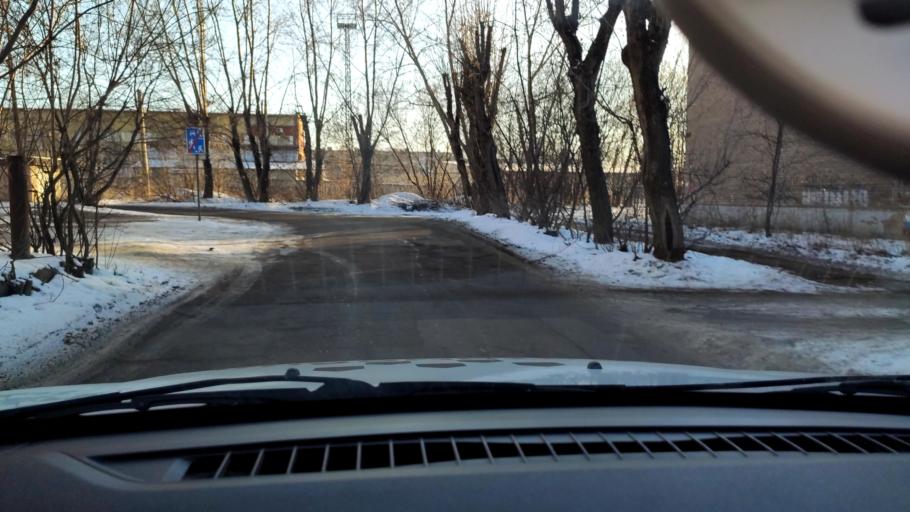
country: RU
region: Perm
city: Overyata
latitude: 58.0007
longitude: 55.9301
